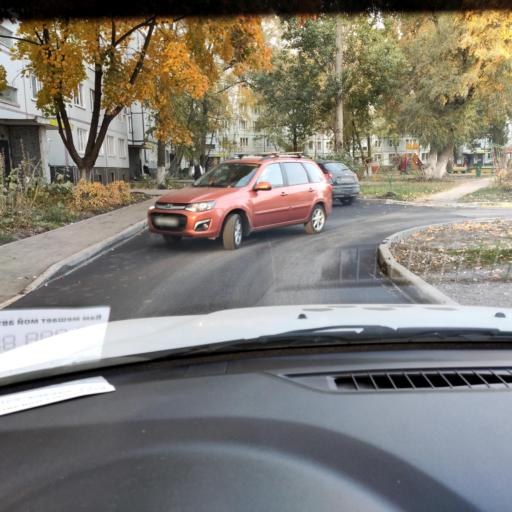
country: RU
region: Samara
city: Tol'yatti
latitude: 53.5058
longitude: 49.4345
